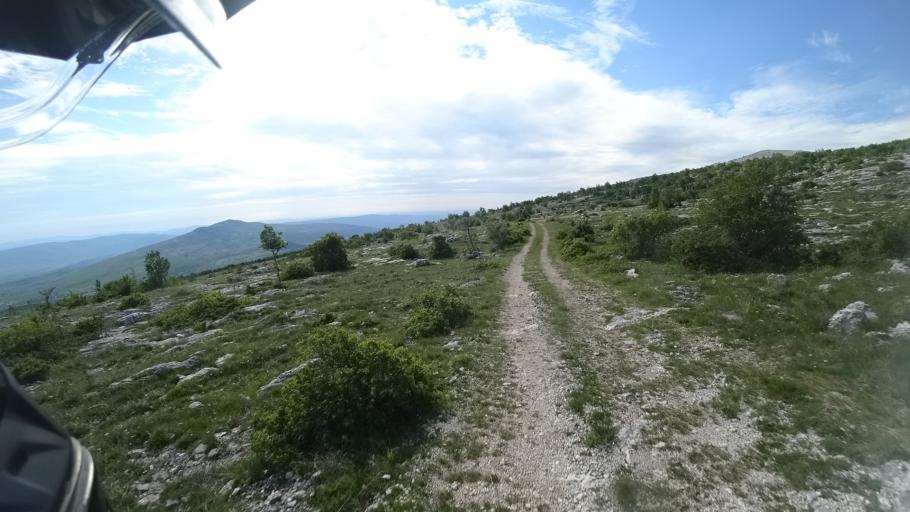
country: HR
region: Splitsko-Dalmatinska
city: Hrvace
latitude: 43.7868
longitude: 16.4335
